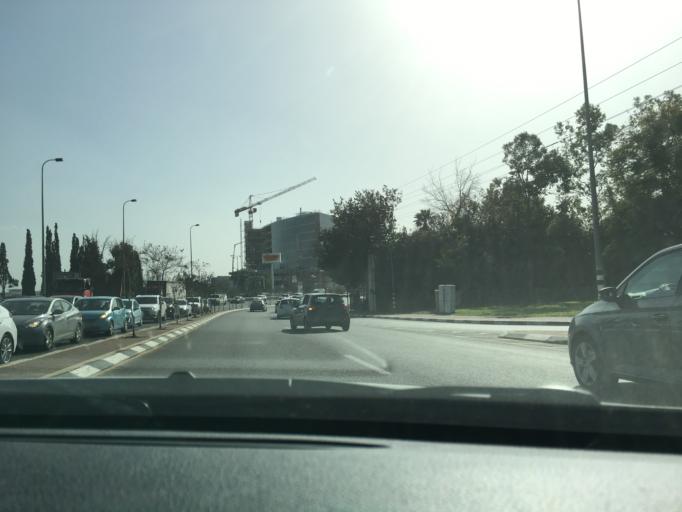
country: IL
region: Central District
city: Kfar Saba
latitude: 32.1704
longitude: 34.9287
